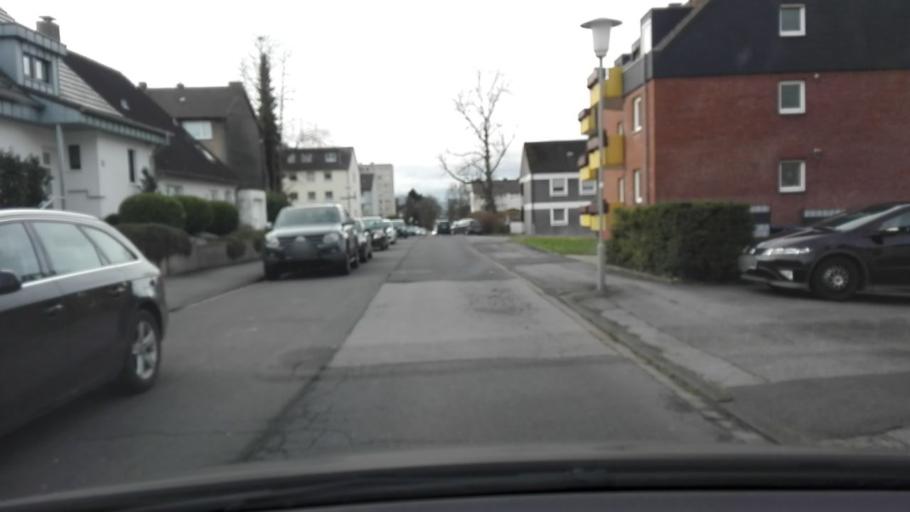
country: DE
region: North Rhine-Westphalia
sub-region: Regierungsbezirk Arnsberg
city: Unna
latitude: 51.5401
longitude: 7.6831
